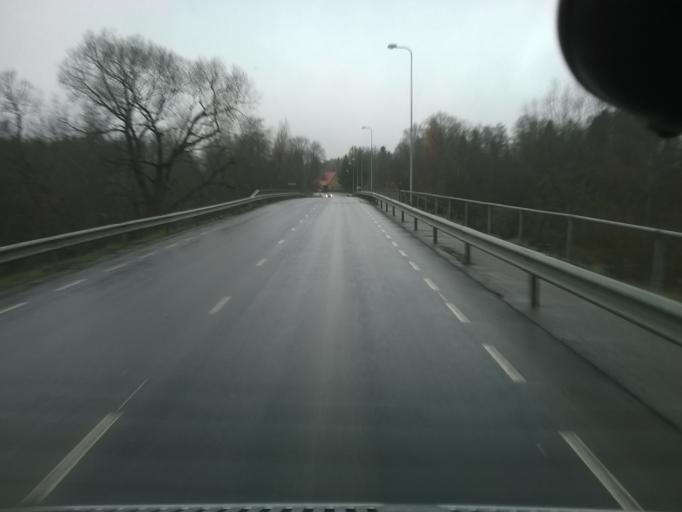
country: EE
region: Harju
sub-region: Saku vald
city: Saku
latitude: 59.2334
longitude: 24.6818
